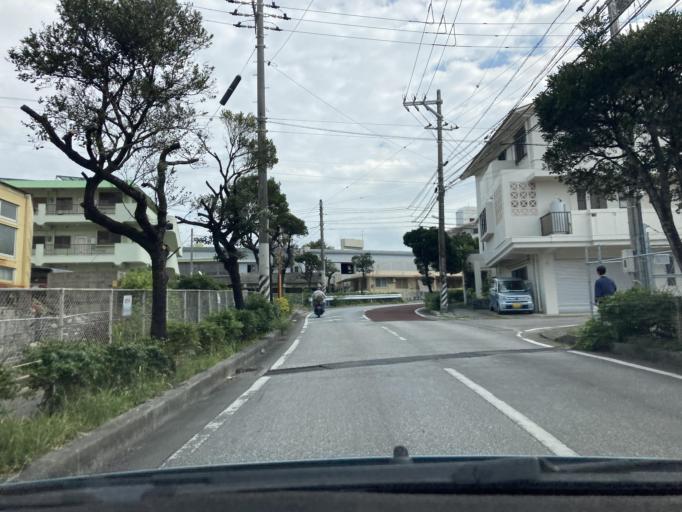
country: JP
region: Okinawa
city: Tomigusuku
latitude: 26.1905
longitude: 127.6929
